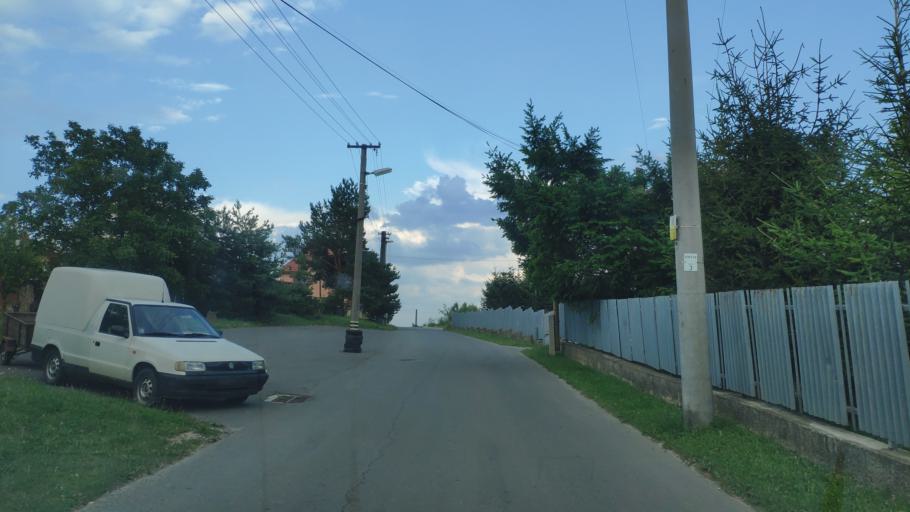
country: SK
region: Kosicky
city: Medzev
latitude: 48.7066
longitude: 20.9769
